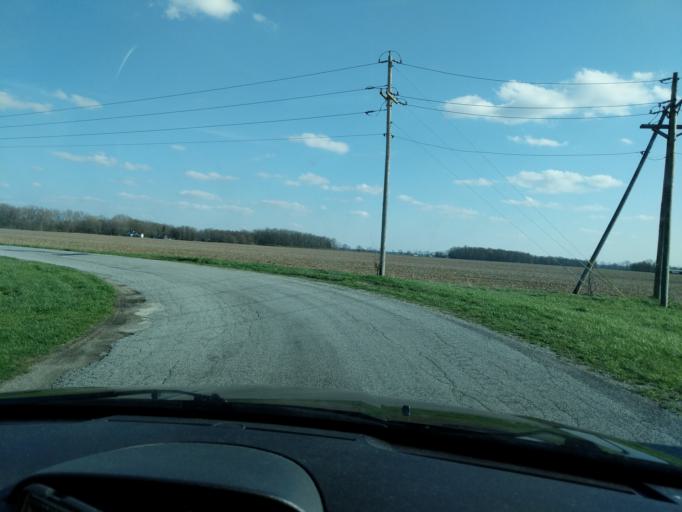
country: US
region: Ohio
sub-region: Champaign County
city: Urbana
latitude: 40.1379
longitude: -83.8159
